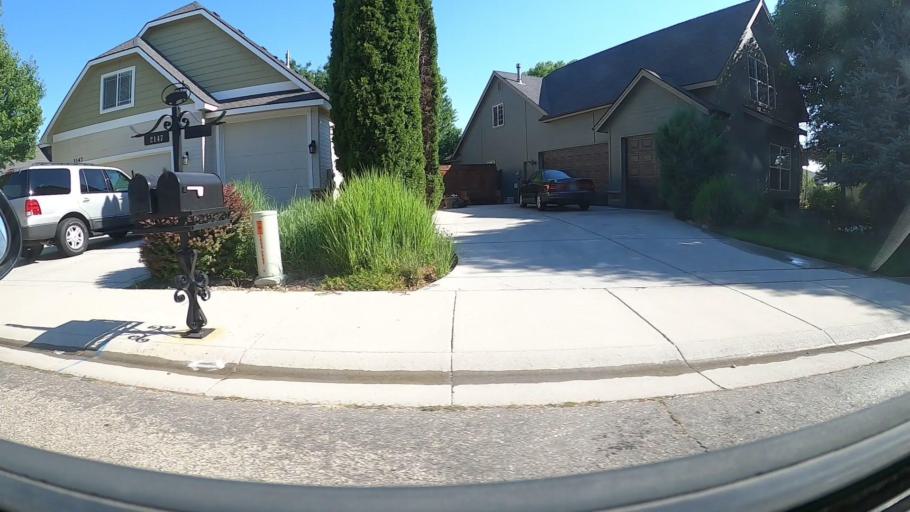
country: US
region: Idaho
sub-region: Ada County
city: Meridian
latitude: 43.6317
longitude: -116.3679
